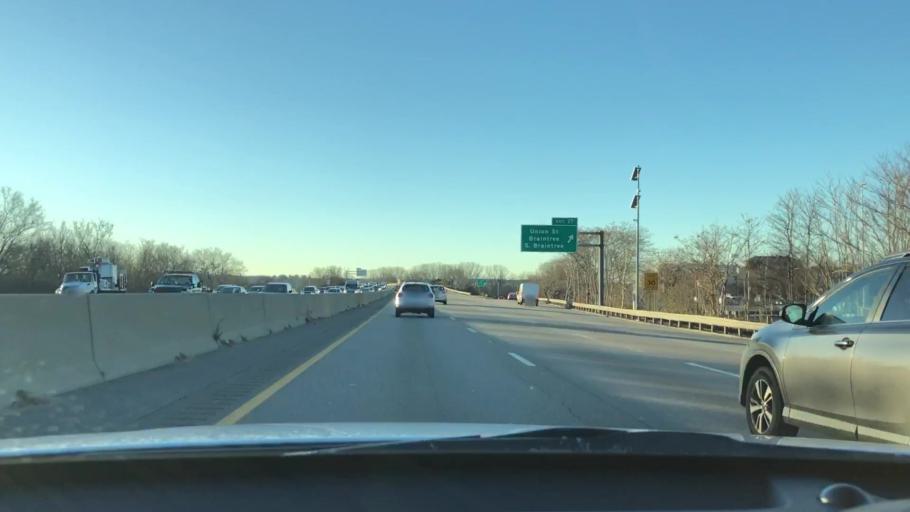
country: US
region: Massachusetts
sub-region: Norfolk County
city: Braintree
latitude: 42.2144
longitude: -70.9971
